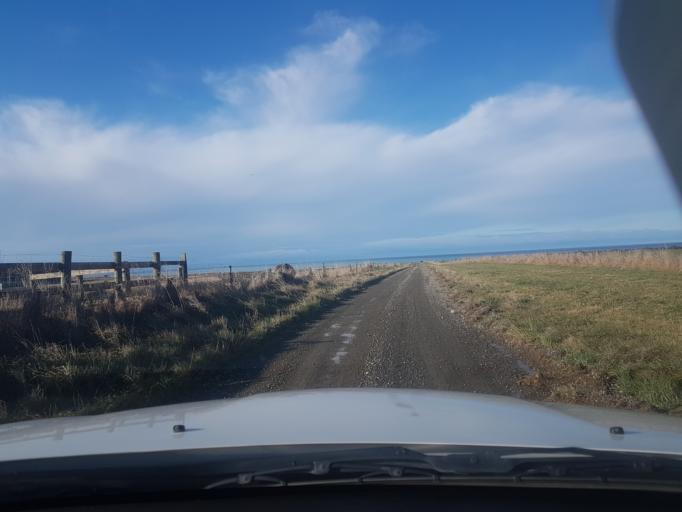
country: NZ
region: Canterbury
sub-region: Timaru District
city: Timaru
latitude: -44.4635
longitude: 171.2369
